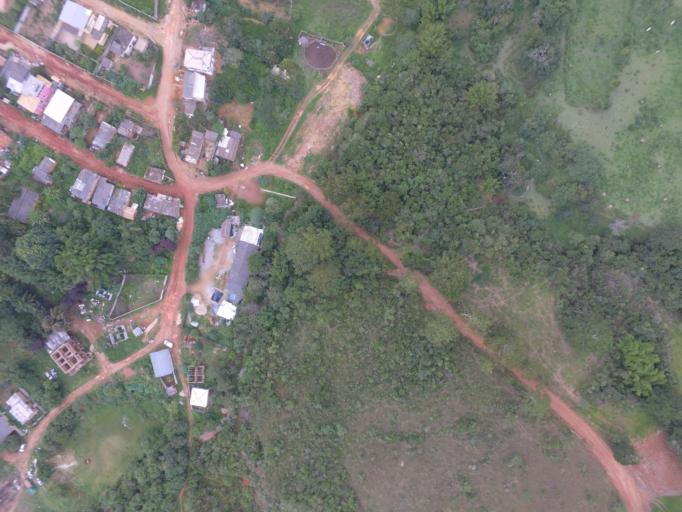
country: BR
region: Minas Gerais
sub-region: Tiradentes
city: Tiradentes
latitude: -21.0484
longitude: -44.0890
